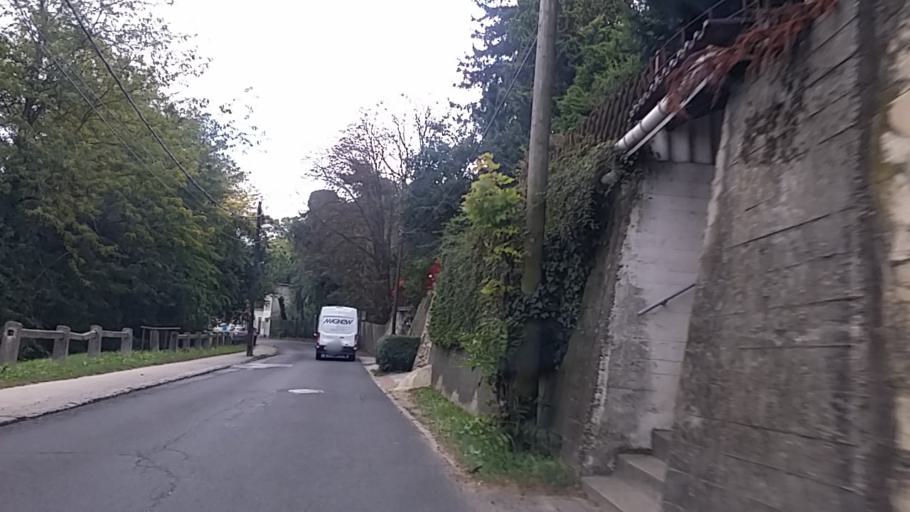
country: HU
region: Pest
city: Urom
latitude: 47.5874
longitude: 19.0416
